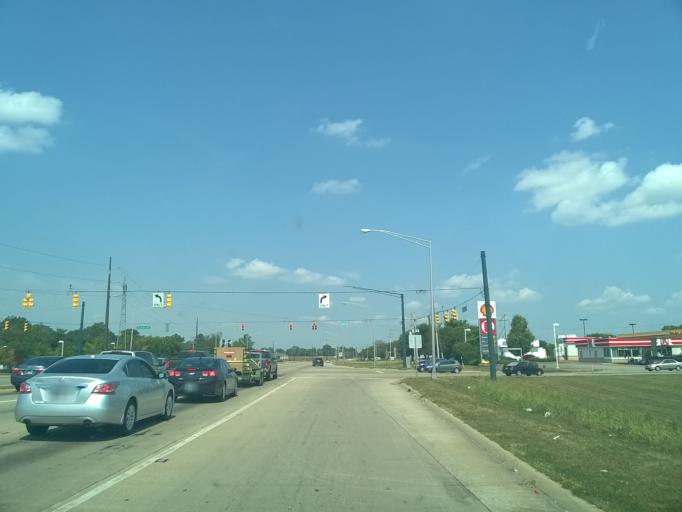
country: US
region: Indiana
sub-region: Hendricks County
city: Plainfield
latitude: 39.6748
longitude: -86.3708
